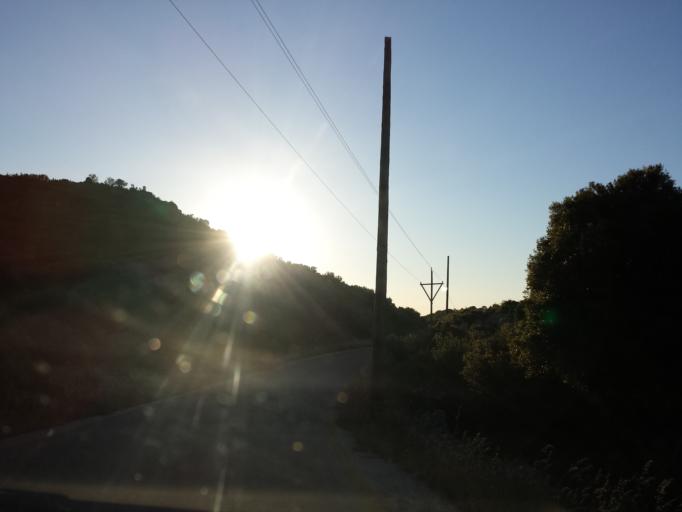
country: GR
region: Ionian Islands
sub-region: Nomos Kerkyras
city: Acharavi
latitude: 39.7500
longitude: 19.8530
